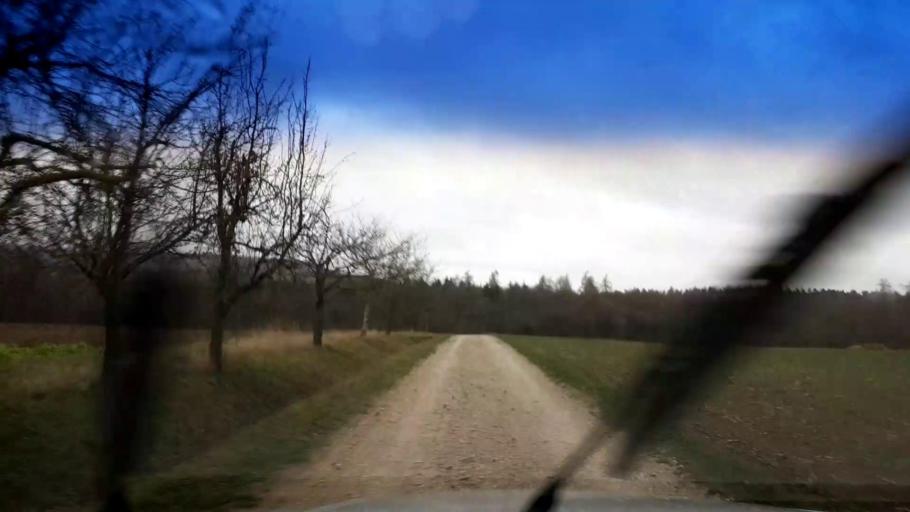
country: DE
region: Bavaria
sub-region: Upper Franconia
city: Litzendorf
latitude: 49.8669
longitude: 11.0317
